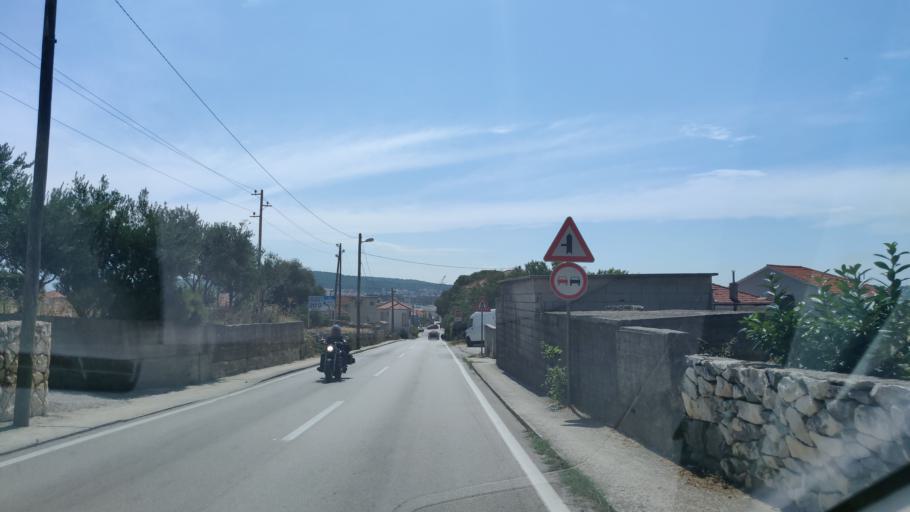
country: HR
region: Splitsko-Dalmatinska
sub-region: Grad Trogir
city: Trogir
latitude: 43.5199
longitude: 16.2273
